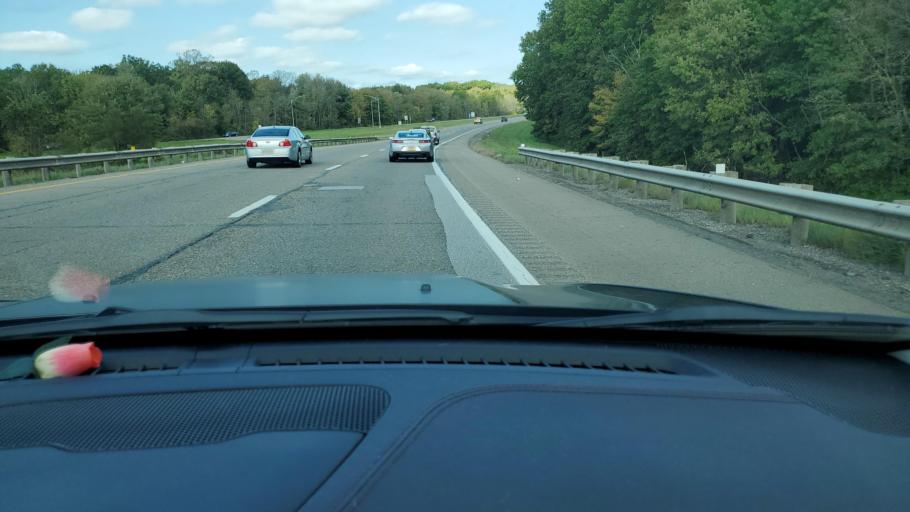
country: US
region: Ohio
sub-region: Trumbull County
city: Howland Center
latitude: 41.2410
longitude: -80.7612
